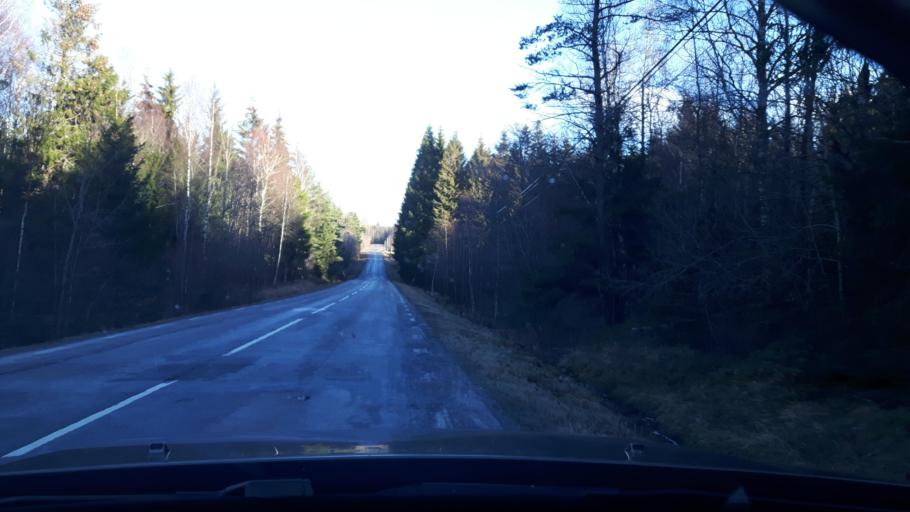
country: SE
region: Vaestra Goetaland
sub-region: Munkedals Kommun
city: Munkedal
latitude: 58.5243
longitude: 11.6877
